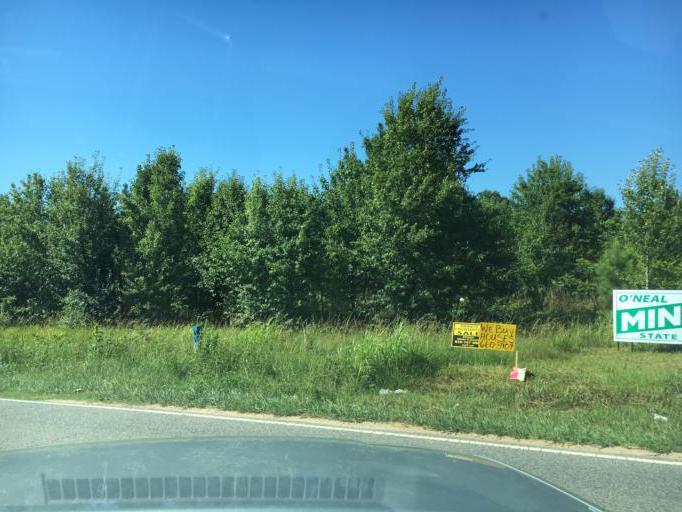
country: US
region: South Carolina
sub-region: Spartanburg County
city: Spartanburg
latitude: 34.9822
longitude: -81.8735
